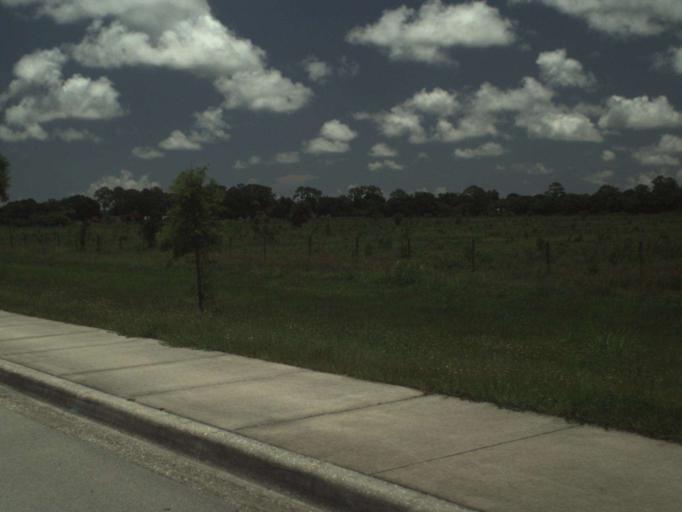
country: US
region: Florida
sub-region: Indian River County
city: West Vero Corridor
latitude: 27.6391
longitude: -80.4788
